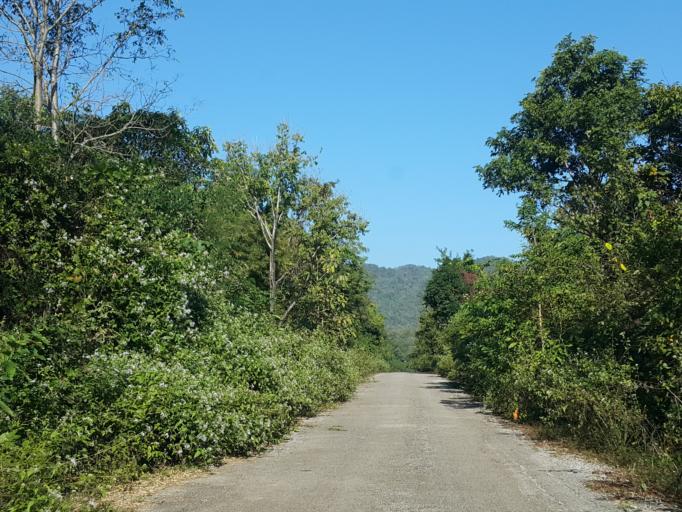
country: TH
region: Lampang
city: Mae Mo
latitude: 18.3043
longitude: 99.6623
